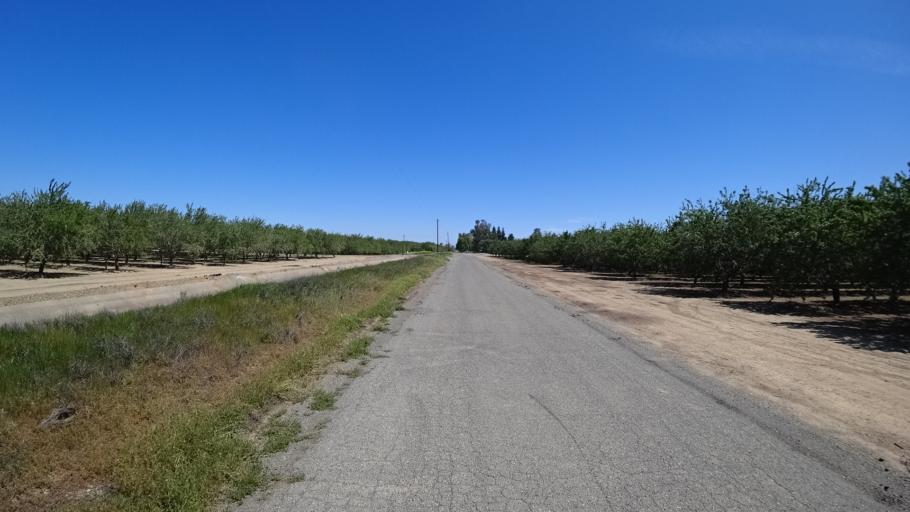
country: US
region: California
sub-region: Glenn County
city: Orland
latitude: 39.7322
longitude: -122.1161
